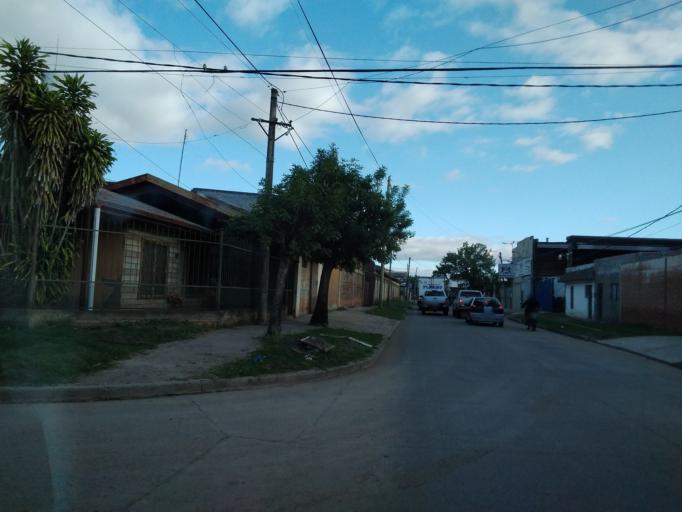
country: AR
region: Corrientes
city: Corrientes
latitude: -27.4781
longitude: -58.8073
